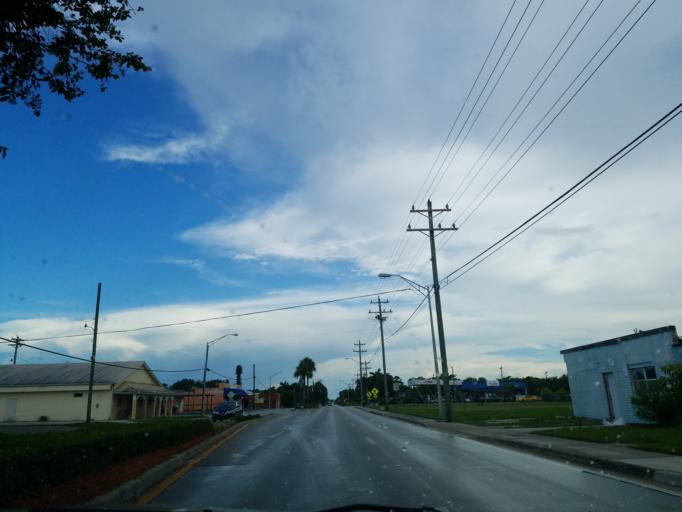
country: US
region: Florida
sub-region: Collier County
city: Immokalee
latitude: 26.4143
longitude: -81.4174
